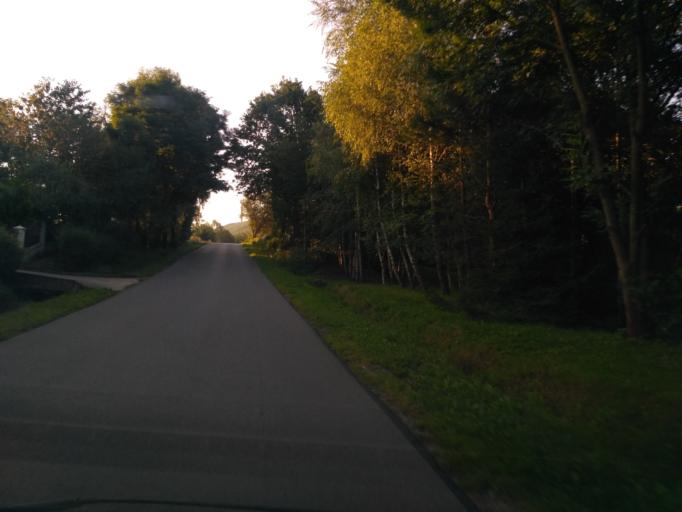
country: PL
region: Subcarpathian Voivodeship
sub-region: Powiat krosnienski
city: Odrzykon
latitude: 49.7682
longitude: 21.7879
